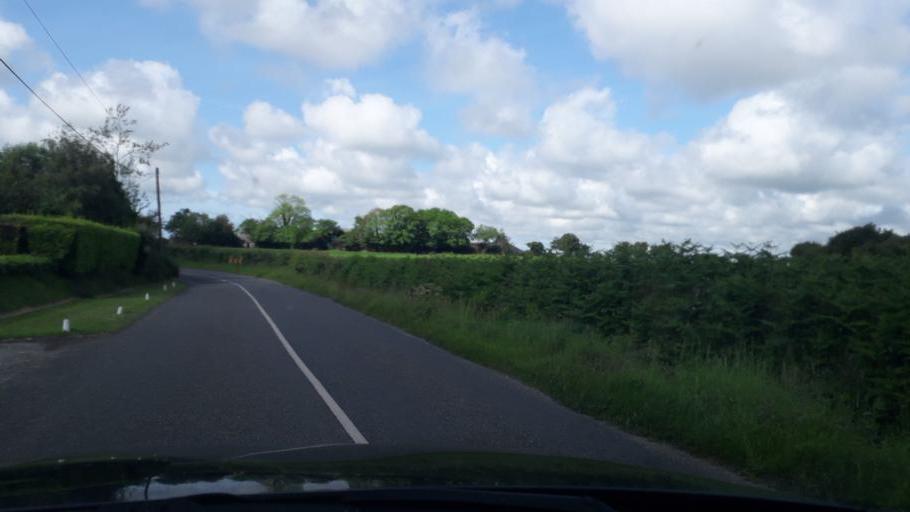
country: IE
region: Leinster
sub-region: Loch Garman
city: Loch Garman
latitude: 52.2816
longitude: -6.5394
